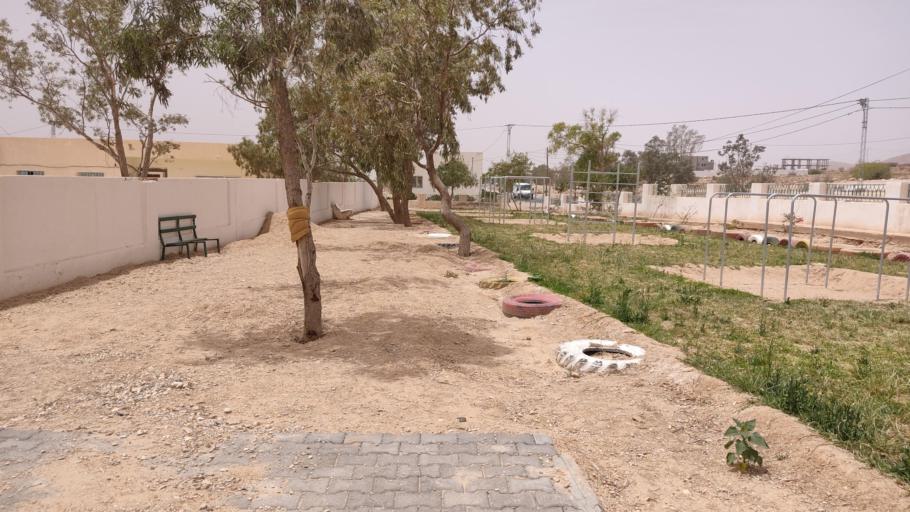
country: TN
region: Gafsa
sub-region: Gafsa Municipality
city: Gafsa
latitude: 34.3408
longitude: 8.9377
